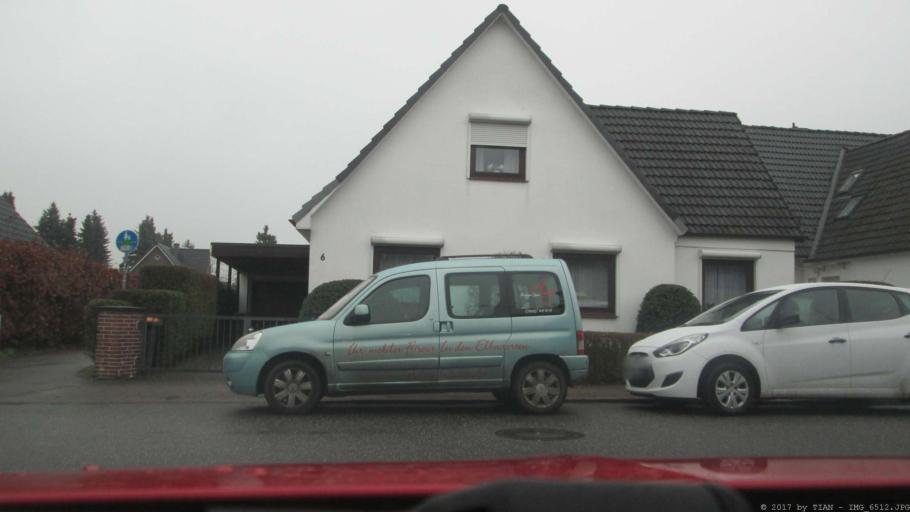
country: DE
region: Schleswig-Holstein
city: Halstenbek
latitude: 53.5784
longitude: 9.8237
